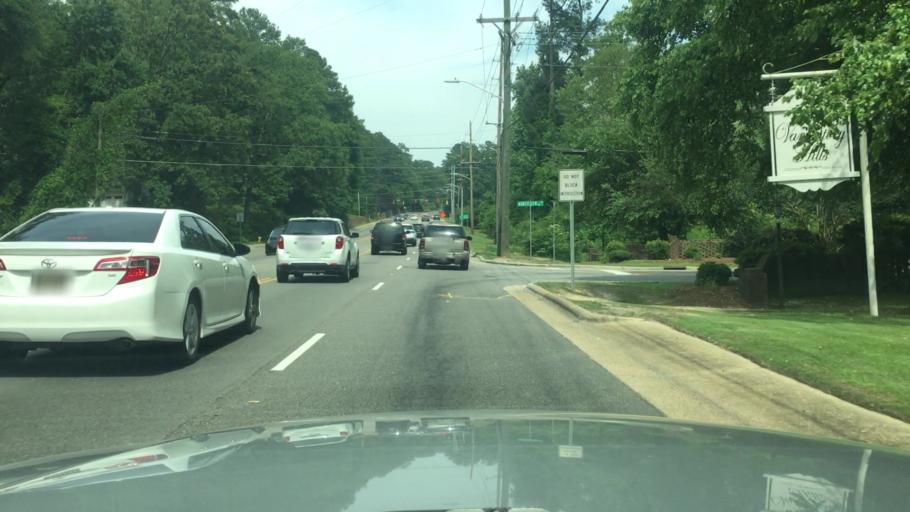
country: US
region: North Carolina
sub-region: Cumberland County
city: Fayetteville
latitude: 35.0638
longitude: -78.9298
